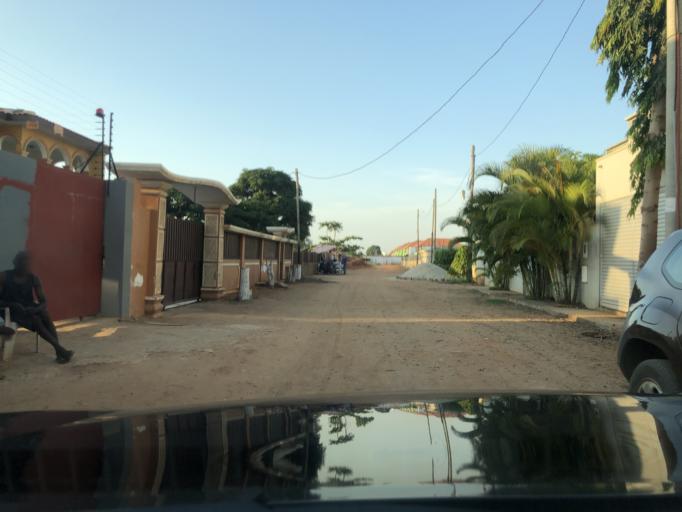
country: AO
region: Luanda
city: Luanda
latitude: -8.9514
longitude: 13.1760
